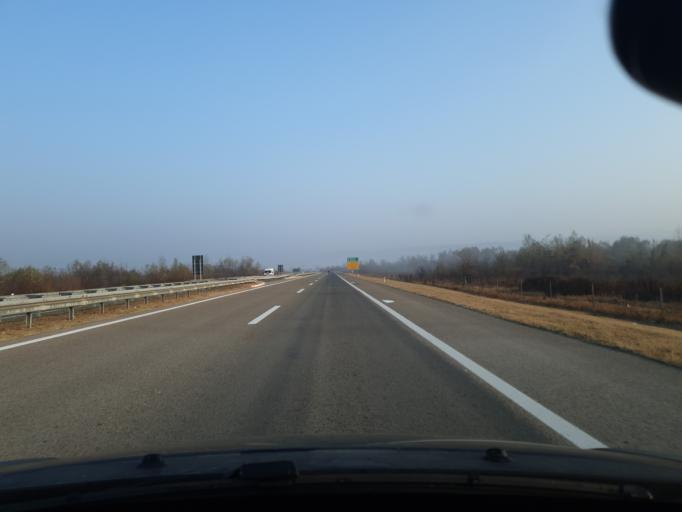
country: RS
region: Central Serbia
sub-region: Jablanicki Okrug
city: Vlasotince
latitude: 42.9587
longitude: 22.0362
